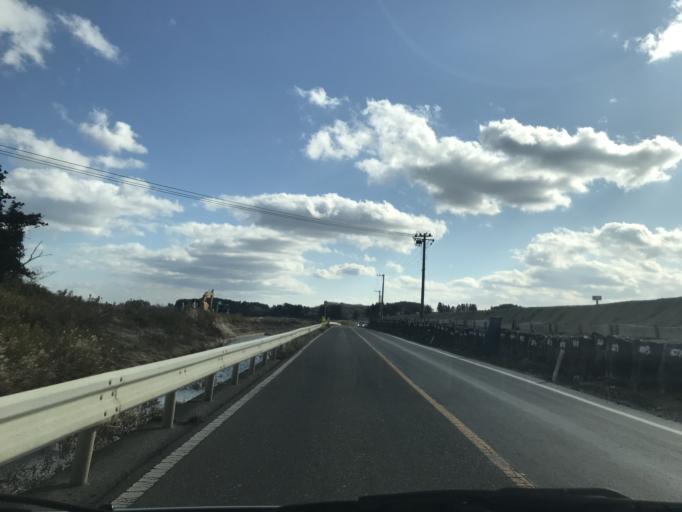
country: JP
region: Miyagi
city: Kogota
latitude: 38.7264
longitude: 141.0616
